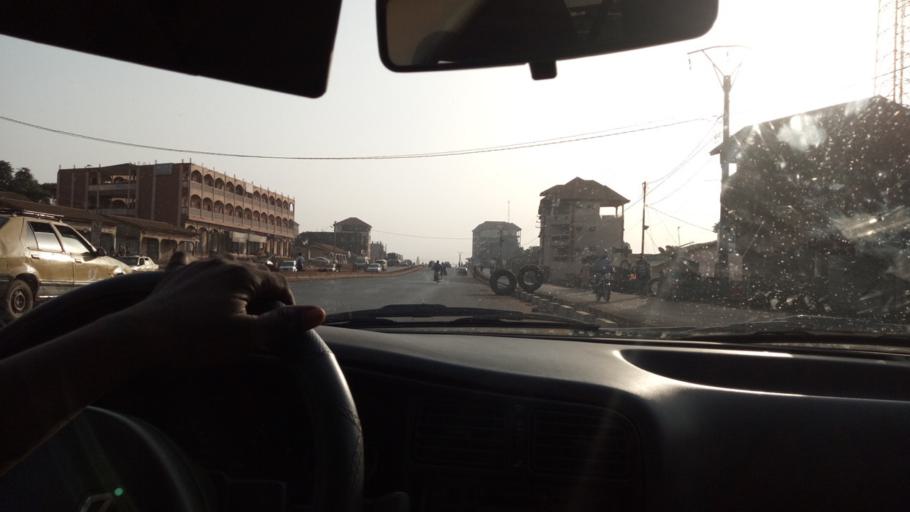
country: GN
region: Kindia
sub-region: Prefecture de Dubreka
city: Dubreka
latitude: 9.6798
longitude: -13.5374
